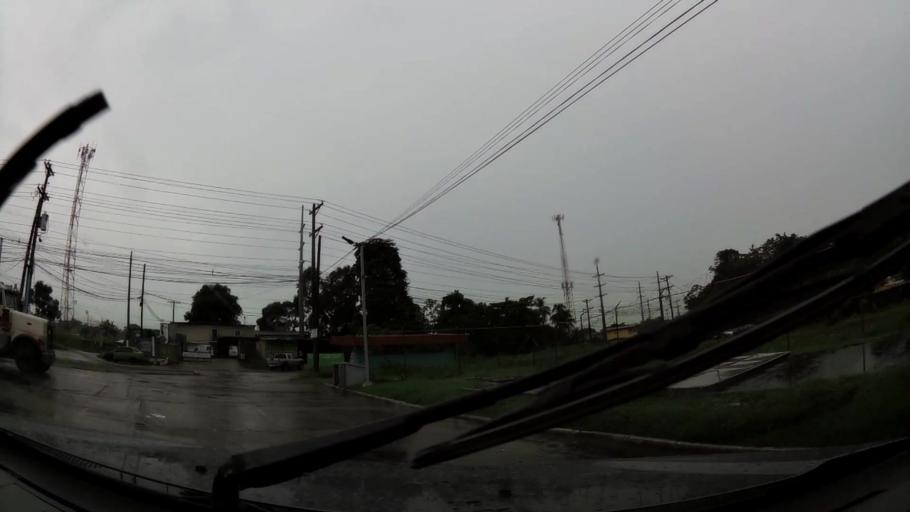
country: PA
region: Colon
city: Cativa
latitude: 9.3630
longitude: -79.8320
